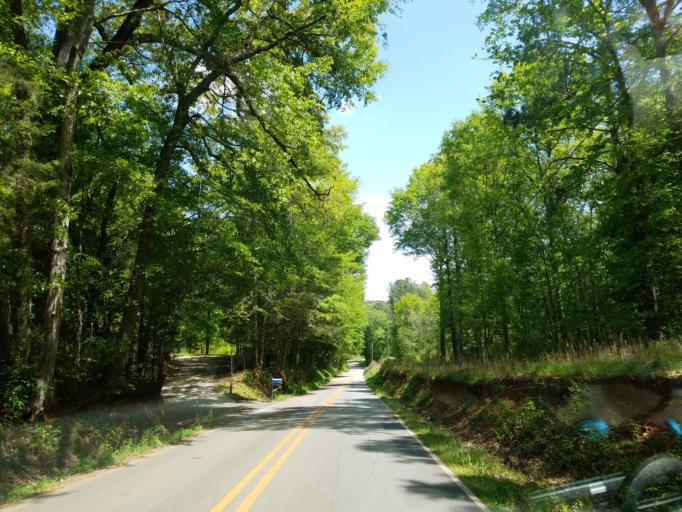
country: US
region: Georgia
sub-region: Butts County
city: Indian Springs
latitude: 33.1588
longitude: -84.0087
